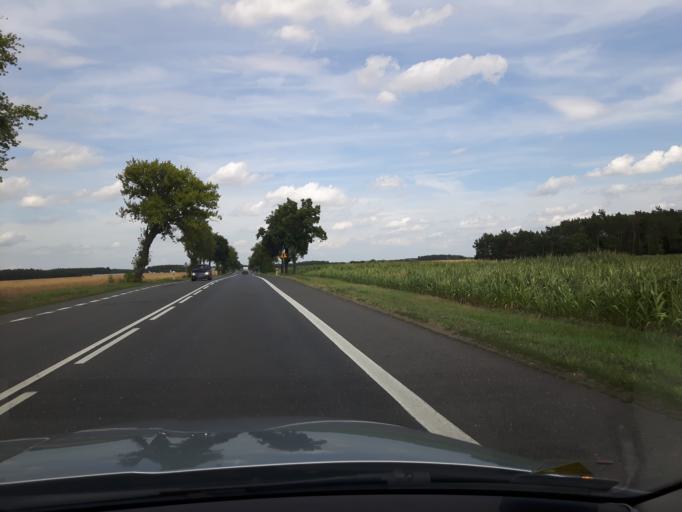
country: PL
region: Masovian Voivodeship
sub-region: Powiat mlawski
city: Strzegowo
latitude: 52.9451
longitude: 20.2840
